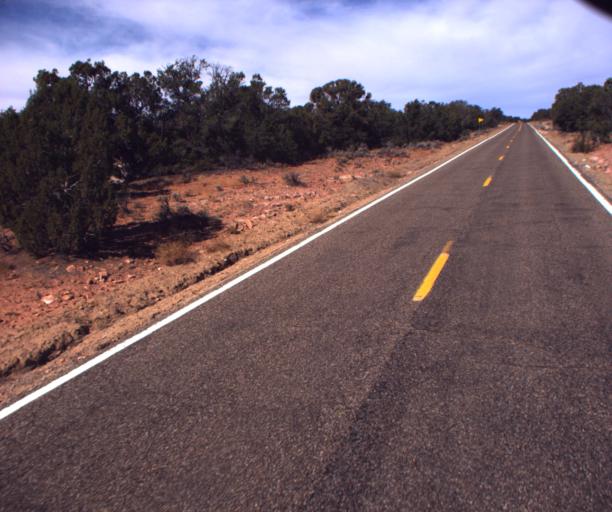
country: US
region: Arizona
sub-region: Navajo County
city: Kayenta
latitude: 36.6160
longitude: -110.5032
